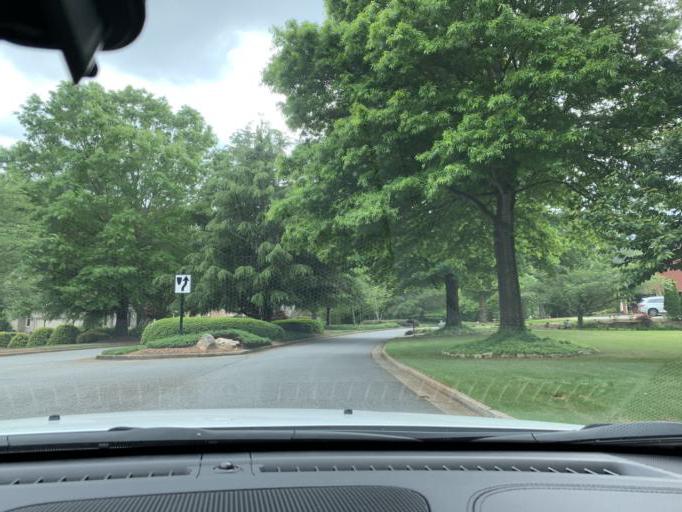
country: US
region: Georgia
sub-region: Gwinnett County
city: Suwanee
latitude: 34.1029
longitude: -84.1156
